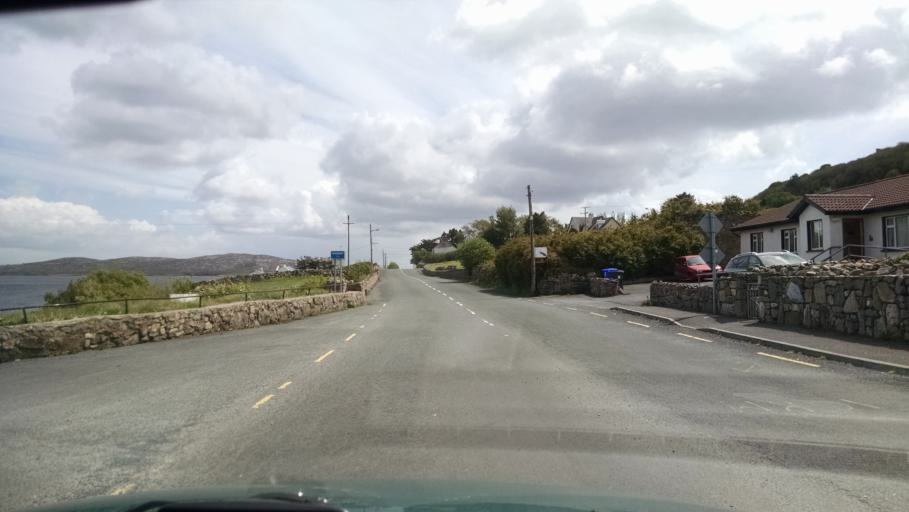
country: IE
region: Connaught
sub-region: County Galway
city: Clifden
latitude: 53.3222
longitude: -9.7370
